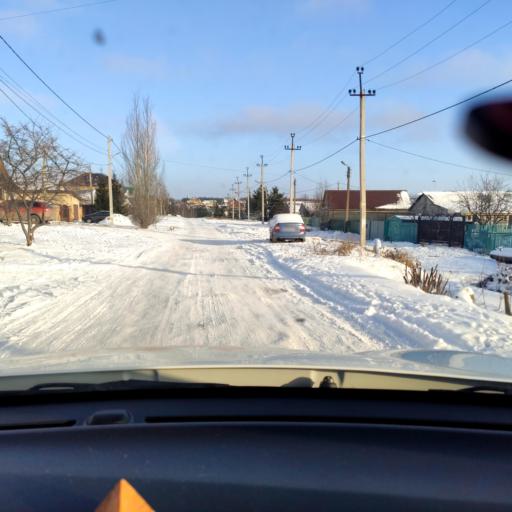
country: RU
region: Tatarstan
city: Vysokaya Gora
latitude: 55.8193
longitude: 49.2614
